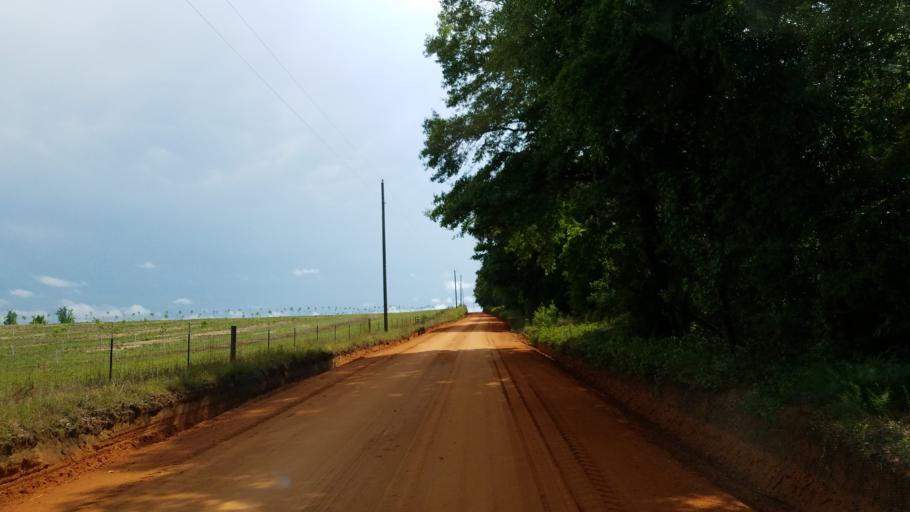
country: US
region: Georgia
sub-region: Houston County
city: Perry
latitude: 32.4529
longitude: -83.7826
